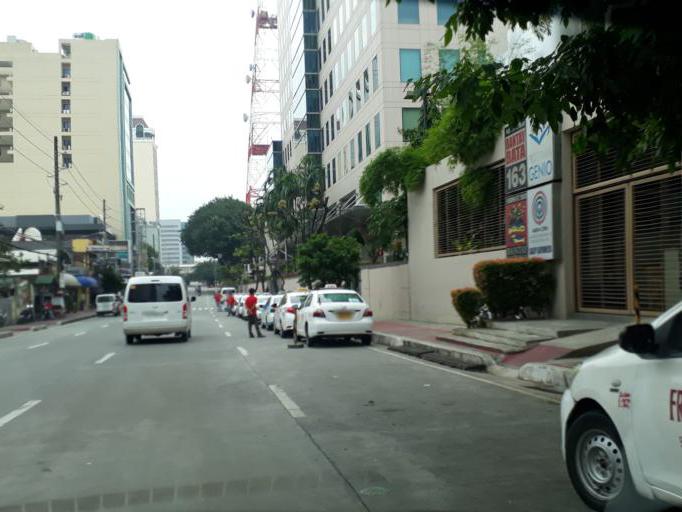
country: PH
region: Calabarzon
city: Del Monte
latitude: 14.6394
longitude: 121.0345
